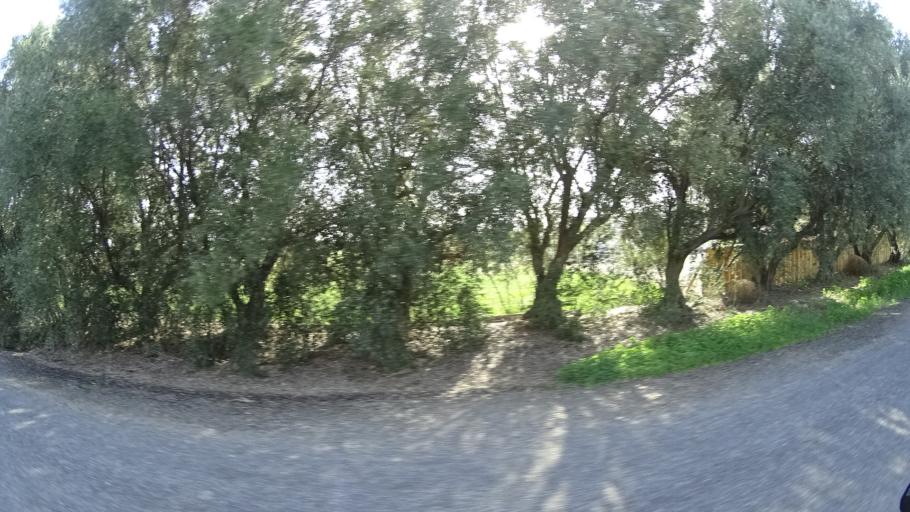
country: US
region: California
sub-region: Glenn County
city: Orland
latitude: 39.7120
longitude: -122.2160
